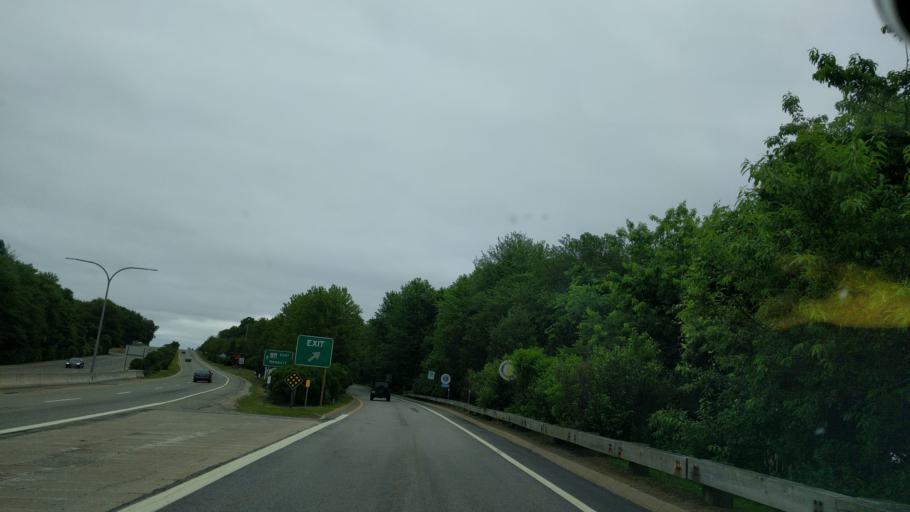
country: US
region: Rhode Island
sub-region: Newport County
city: Jamestown
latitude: 41.5258
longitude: -71.3886
